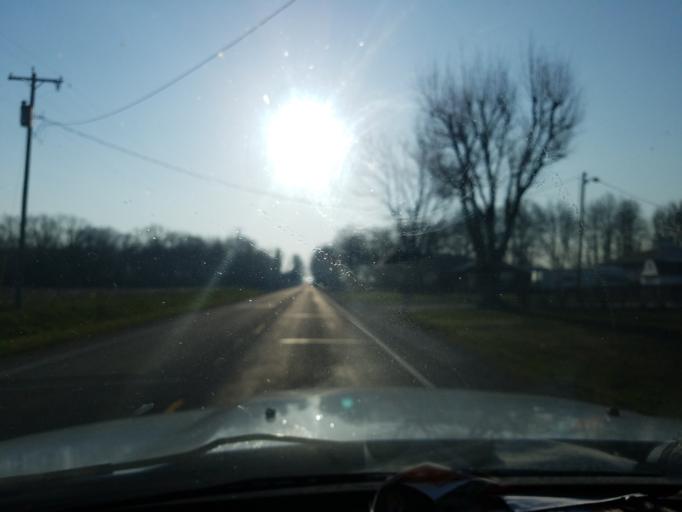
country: US
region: Indiana
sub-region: Vigo County
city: Seelyville
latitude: 39.3895
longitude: -87.2180
